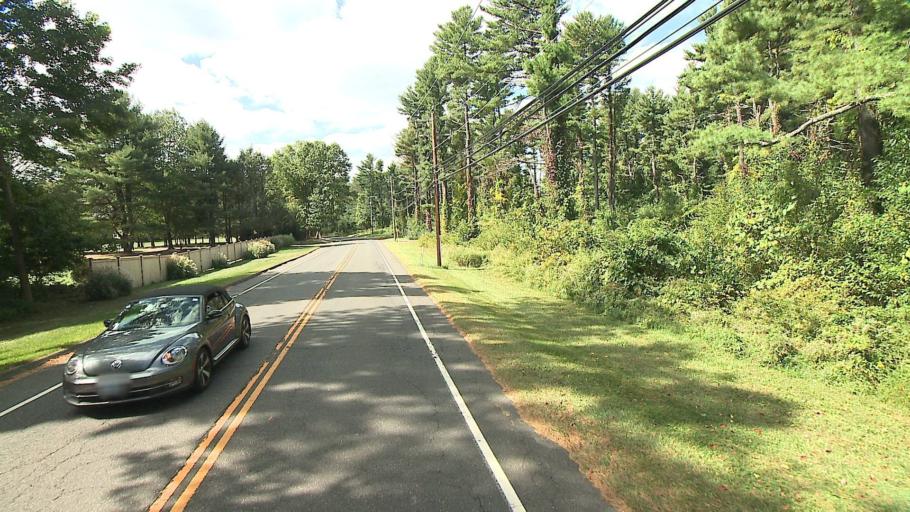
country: US
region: Connecticut
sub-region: Fairfield County
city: Wilton
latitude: 41.1745
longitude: -73.4434
